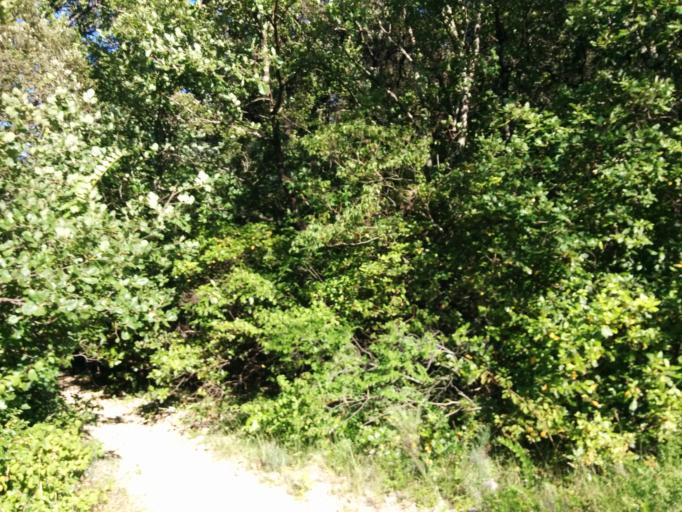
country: FR
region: Languedoc-Roussillon
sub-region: Departement du Gard
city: Bagard
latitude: 44.0901
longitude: 4.0571
